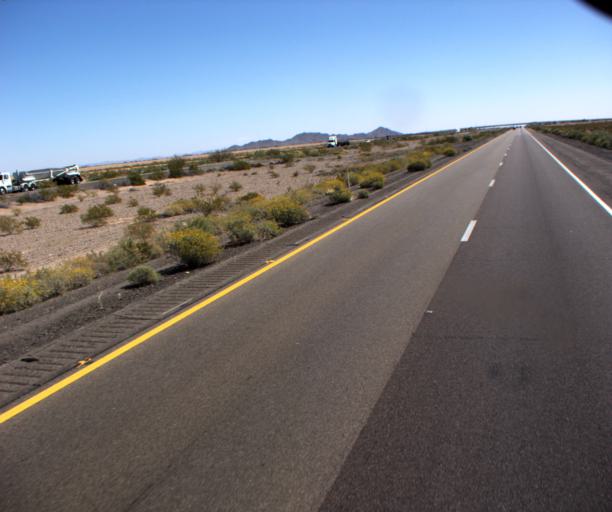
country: US
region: Arizona
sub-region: La Paz County
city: Salome
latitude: 33.5969
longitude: -113.5403
